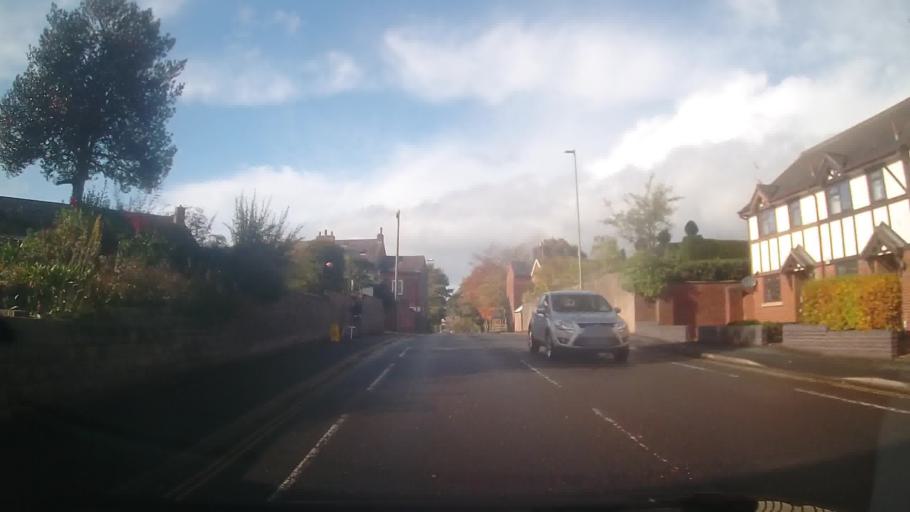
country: GB
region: England
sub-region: Shropshire
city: Whitchurch
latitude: 52.9715
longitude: -2.6809
